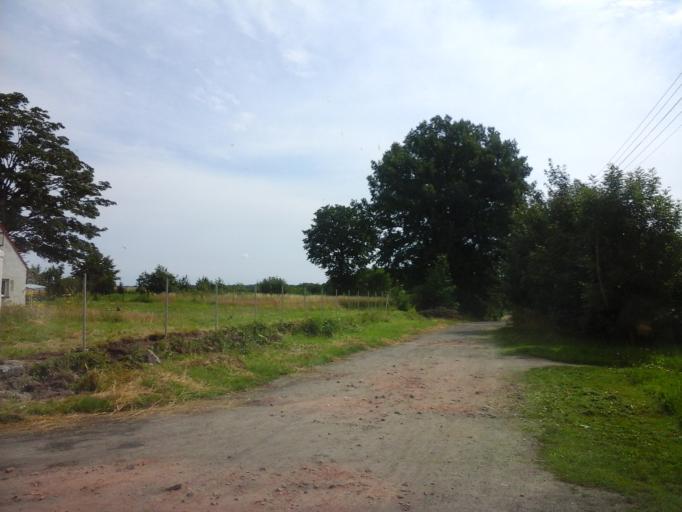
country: PL
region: West Pomeranian Voivodeship
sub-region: Powiat choszczenski
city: Recz
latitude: 53.2638
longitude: 15.6200
